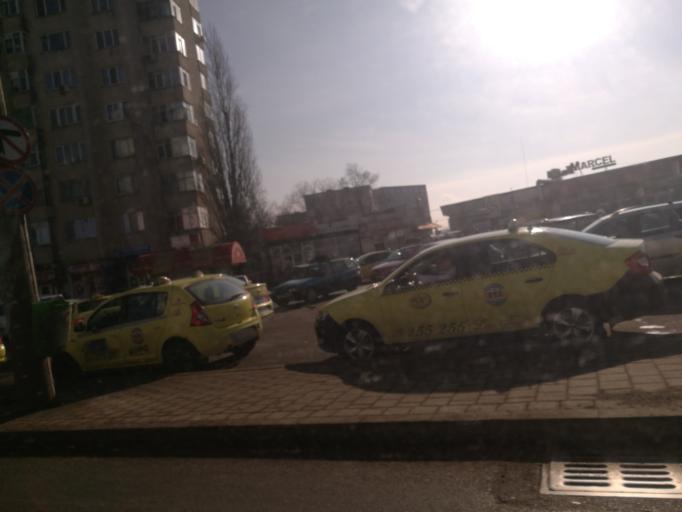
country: RO
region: Iasi
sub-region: Municipiul Iasi
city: Iasi
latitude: 47.1460
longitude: 27.5900
